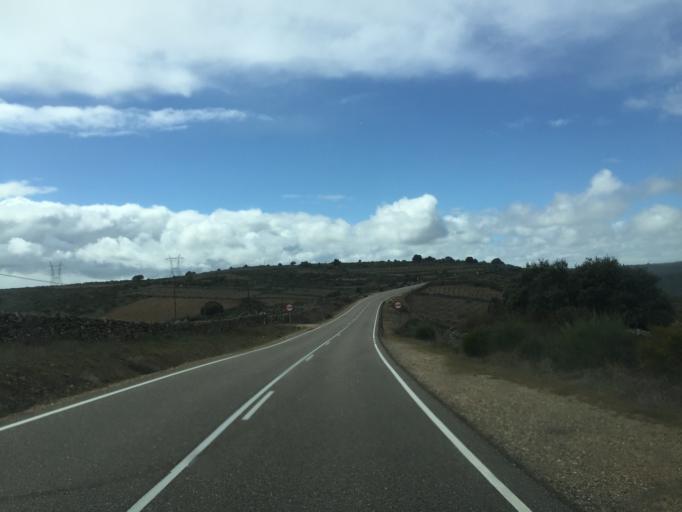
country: ES
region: Castille and Leon
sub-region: Provincia de Zamora
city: Villalcampo
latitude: 41.5065
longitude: -6.0724
